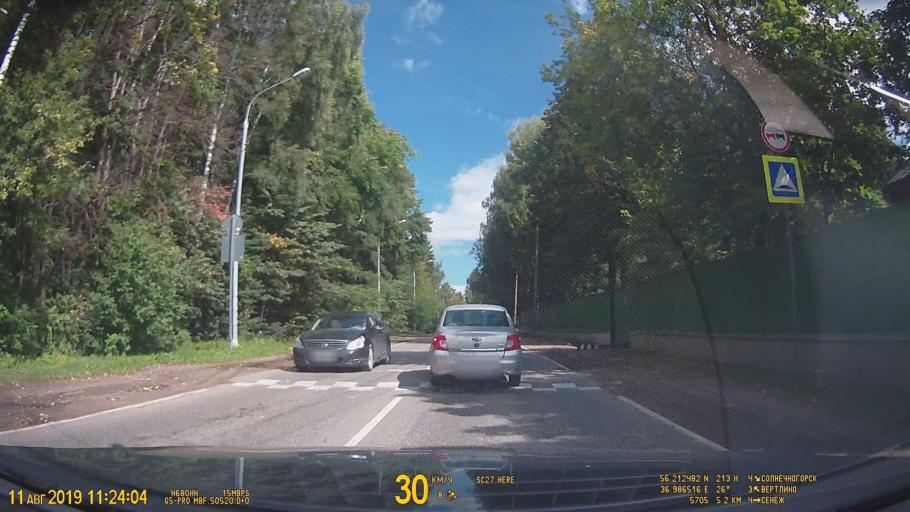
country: RU
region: Moskovskaya
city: Solnechnogorsk
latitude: 56.2125
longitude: 36.9866
